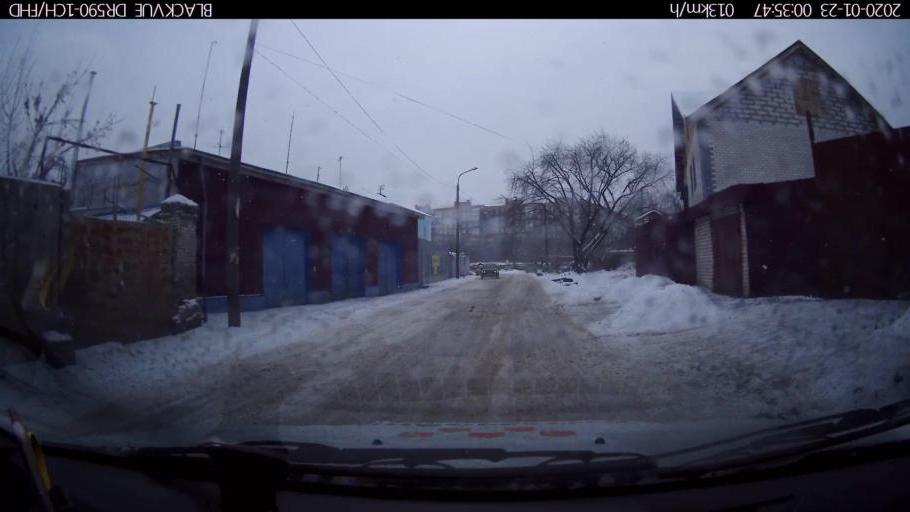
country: RU
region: Nizjnij Novgorod
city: Neklyudovo
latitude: 56.3564
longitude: 43.8536
